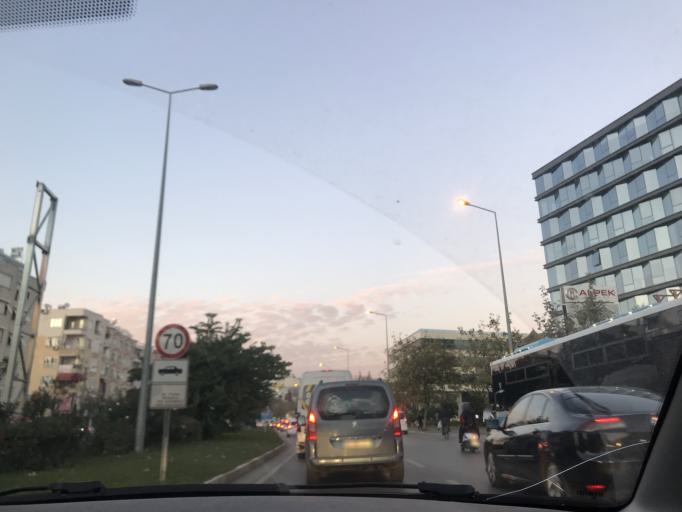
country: TR
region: Antalya
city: Antalya
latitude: 36.9001
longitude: 30.7158
